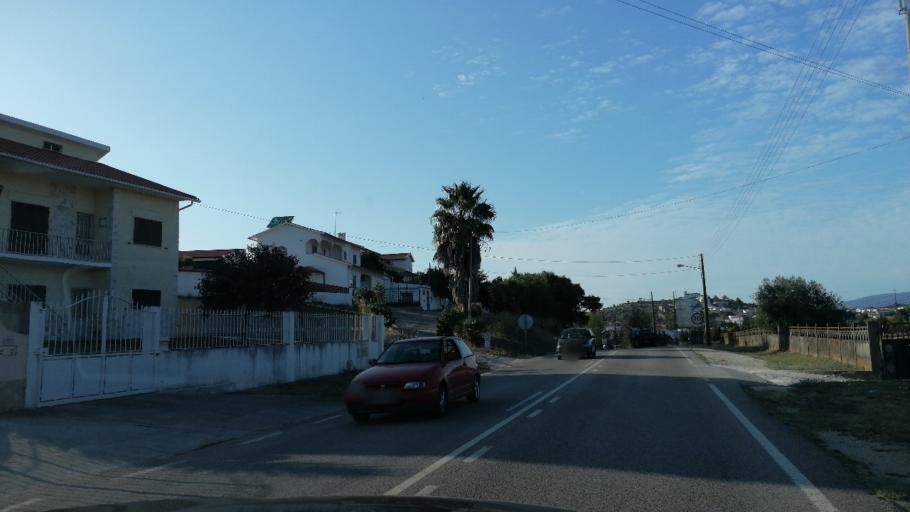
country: PT
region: Santarem
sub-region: Alcanena
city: Alcanena
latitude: 39.3731
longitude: -8.6595
